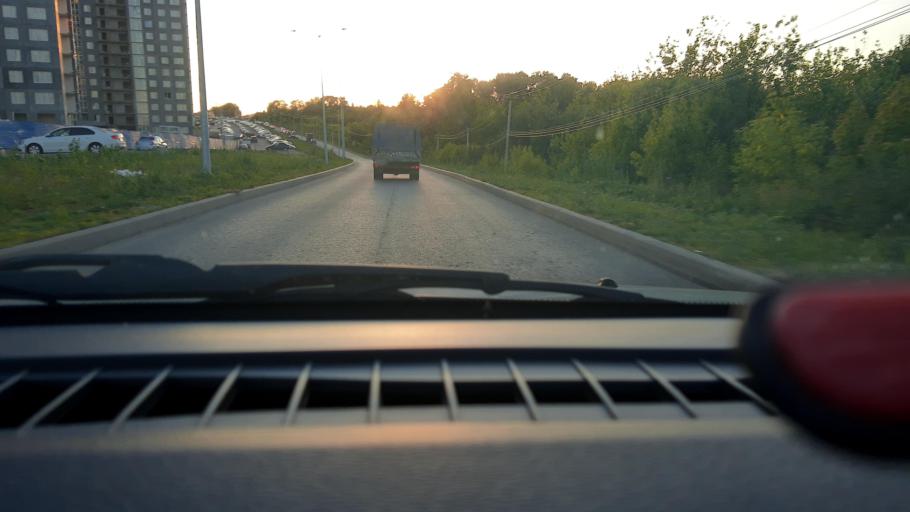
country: RU
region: Nizjnij Novgorod
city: Afonino
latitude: 56.2473
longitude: 44.0525
